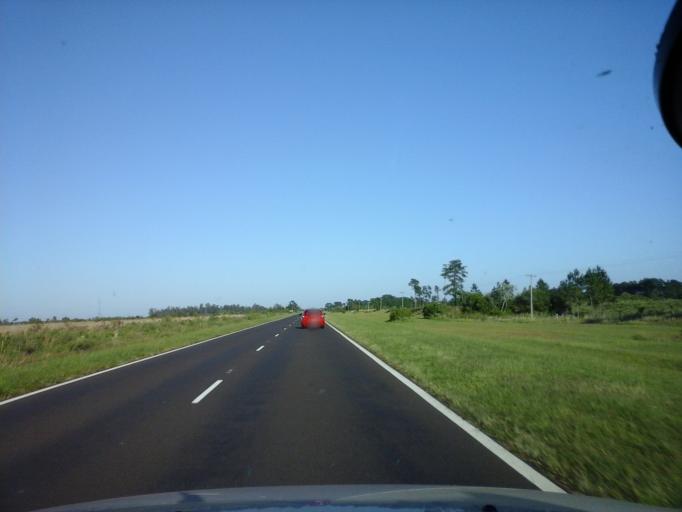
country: AR
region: Corrientes
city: Ita Ibate
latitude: -27.4929
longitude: -57.2703
